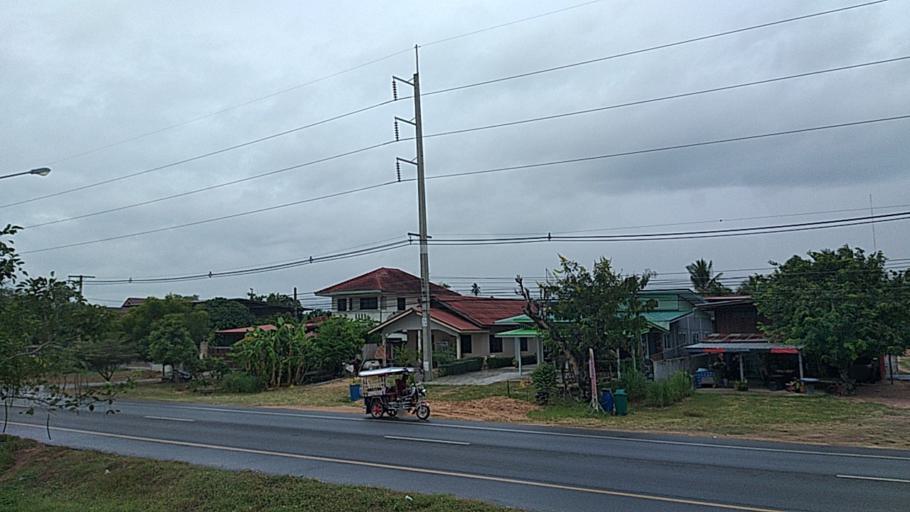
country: TH
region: Maha Sarakham
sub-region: Amphoe Borabue
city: Borabue
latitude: 16.0553
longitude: 103.1331
